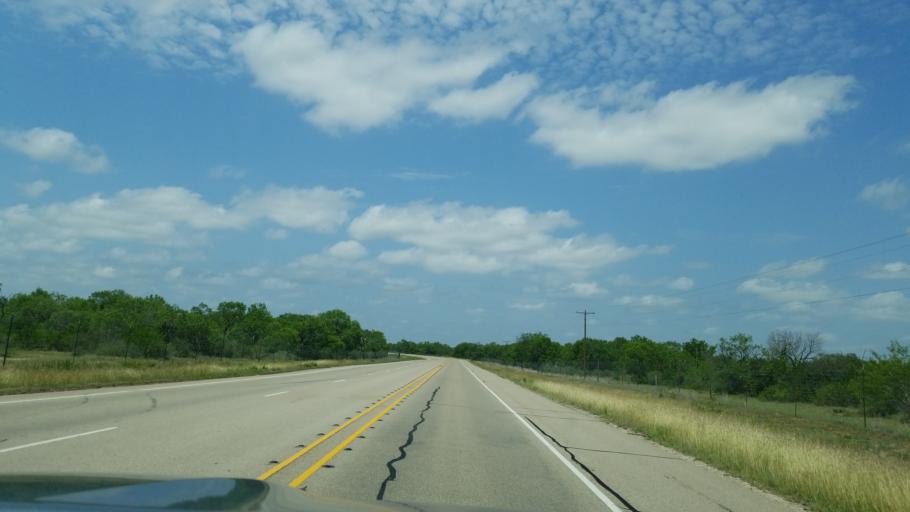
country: US
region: Texas
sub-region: Frio County
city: Pearsall
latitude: 29.0082
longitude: -99.2038
